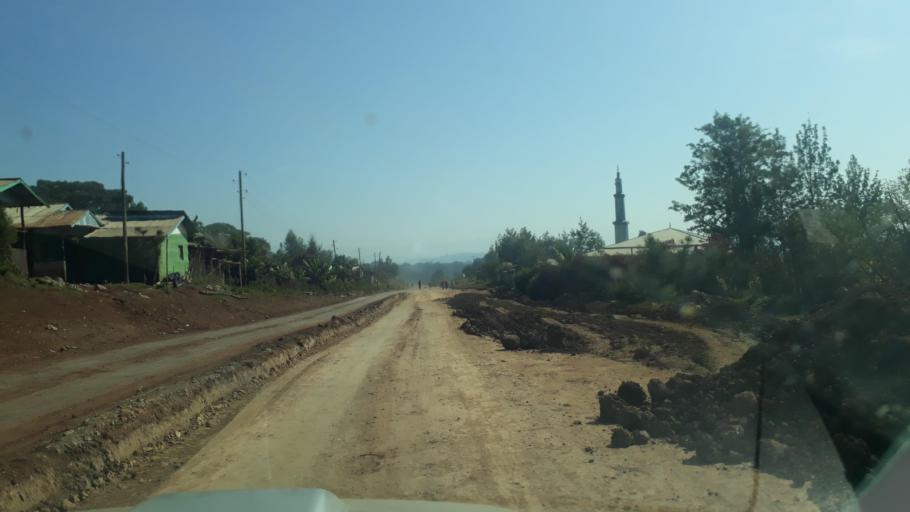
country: ET
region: Oromiya
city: Agaro
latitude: 7.8587
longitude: 36.6406
